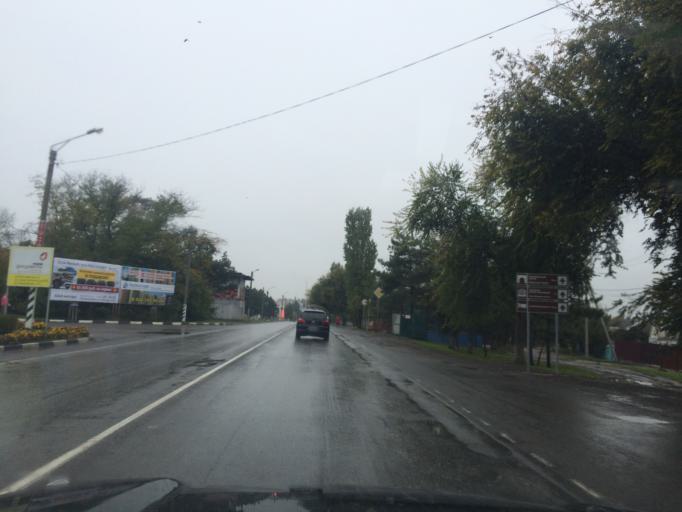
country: RU
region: Rostov
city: Azov
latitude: 47.0884
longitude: 39.4632
